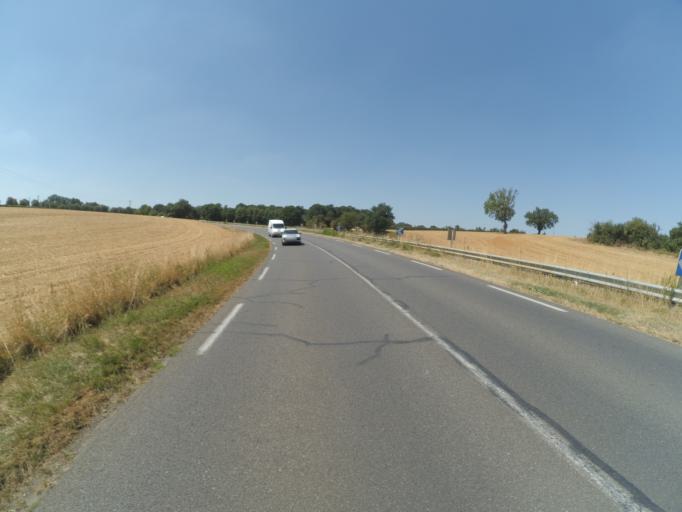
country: FR
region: Poitou-Charentes
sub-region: Departement de la Vienne
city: Lusignan
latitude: 46.4323
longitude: 0.1052
